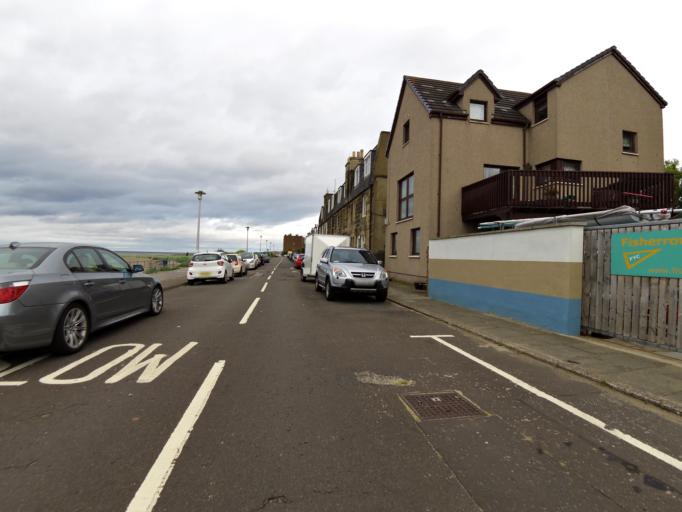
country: GB
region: Scotland
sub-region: East Lothian
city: Musselburgh
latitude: 55.9454
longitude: -3.0643
